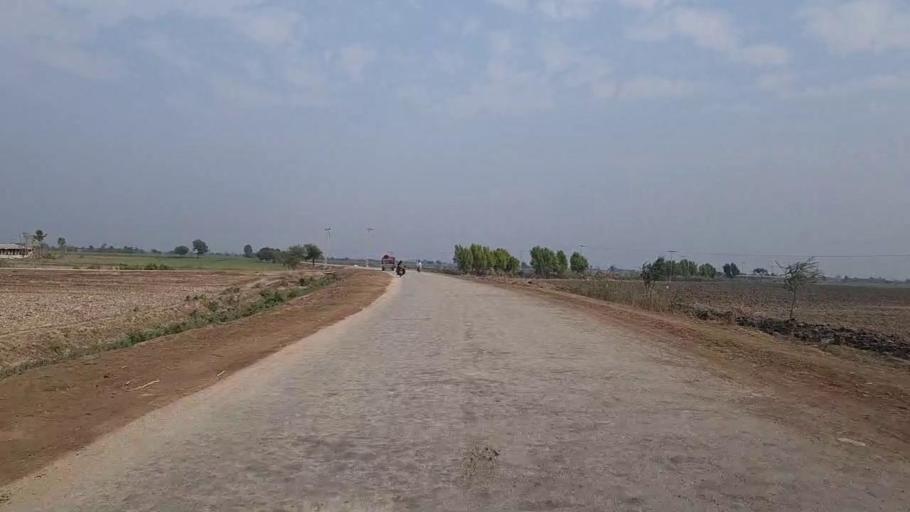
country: PK
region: Sindh
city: Mirwah Gorchani
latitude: 25.3729
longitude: 69.1011
